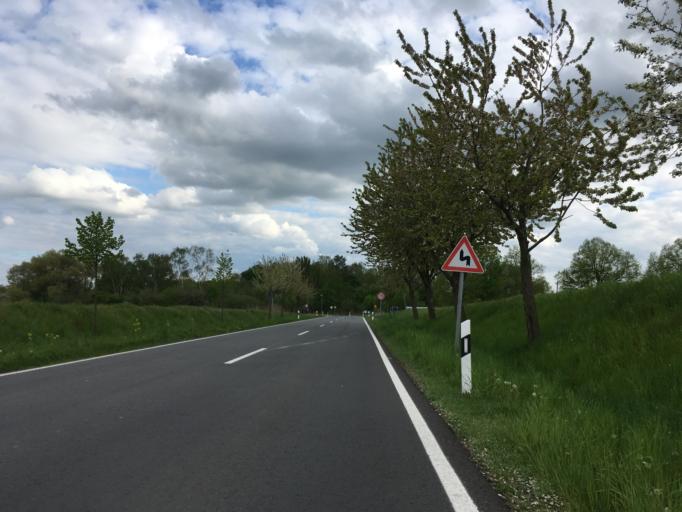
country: DE
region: Brandenburg
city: Bernau bei Berlin
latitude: 52.6471
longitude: 13.6070
